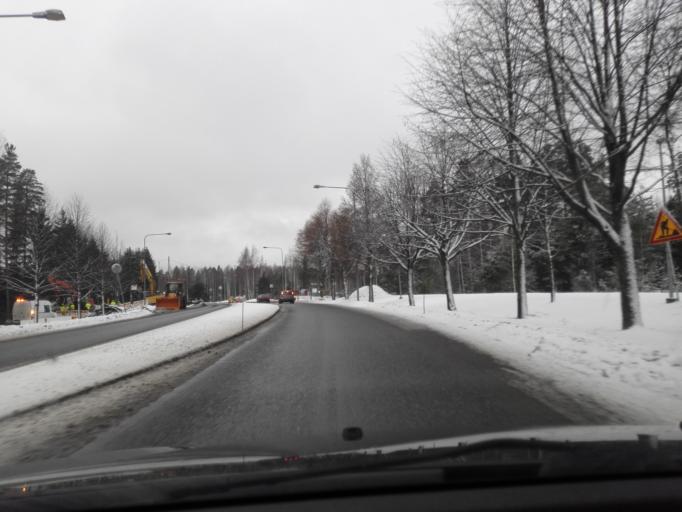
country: FI
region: Uusimaa
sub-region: Helsinki
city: Vantaa
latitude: 60.2844
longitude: 25.0702
